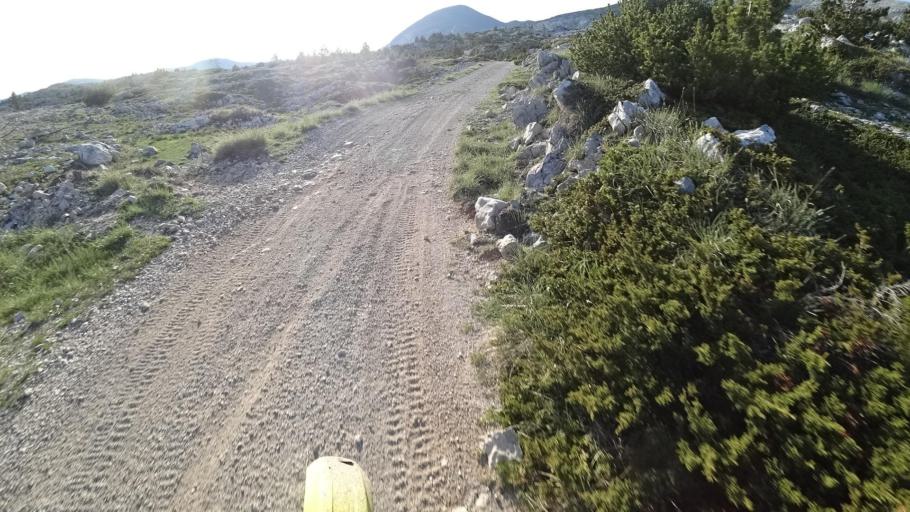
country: BA
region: Federation of Bosnia and Herzegovina
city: Kocerin
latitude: 43.5742
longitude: 17.5369
